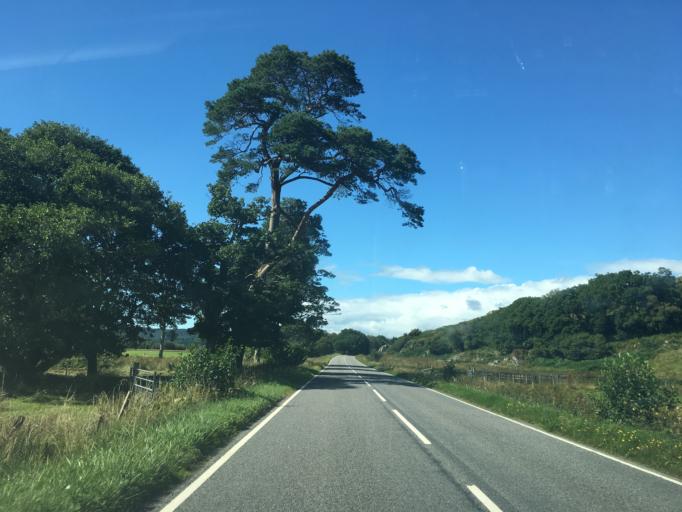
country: GB
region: Scotland
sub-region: Argyll and Bute
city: Lochgilphead
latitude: 56.0901
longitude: -5.4702
